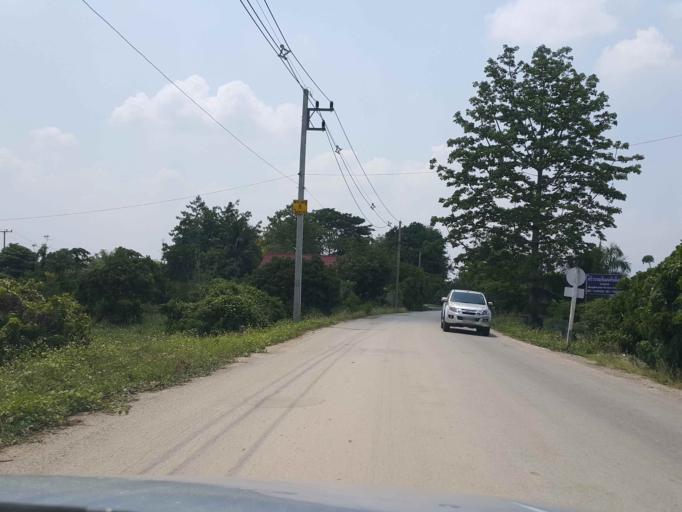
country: TH
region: Chiang Mai
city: Saraphi
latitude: 18.6757
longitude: 99.0080
